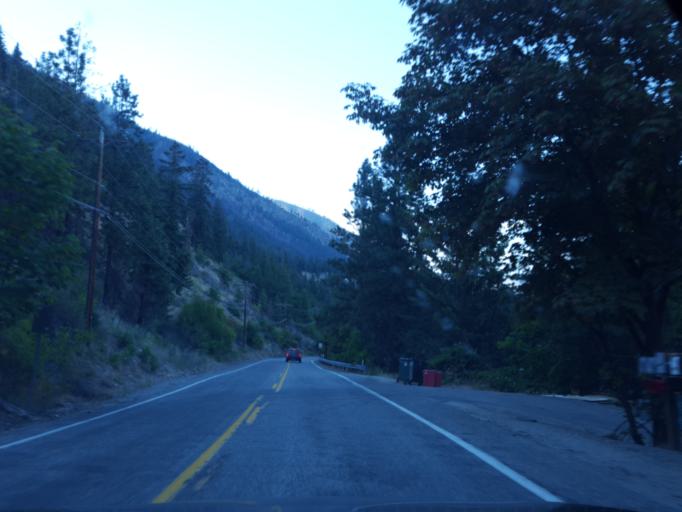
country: US
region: Washington
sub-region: Chelan County
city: Granite Falls
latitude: 47.9042
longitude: -120.2157
